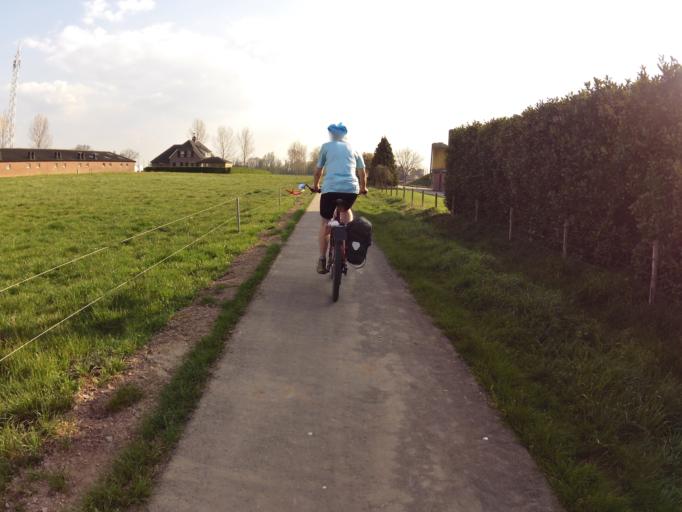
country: NL
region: North Brabant
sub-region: Gemeente Grave
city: Grave
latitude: 51.7778
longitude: 5.7538
